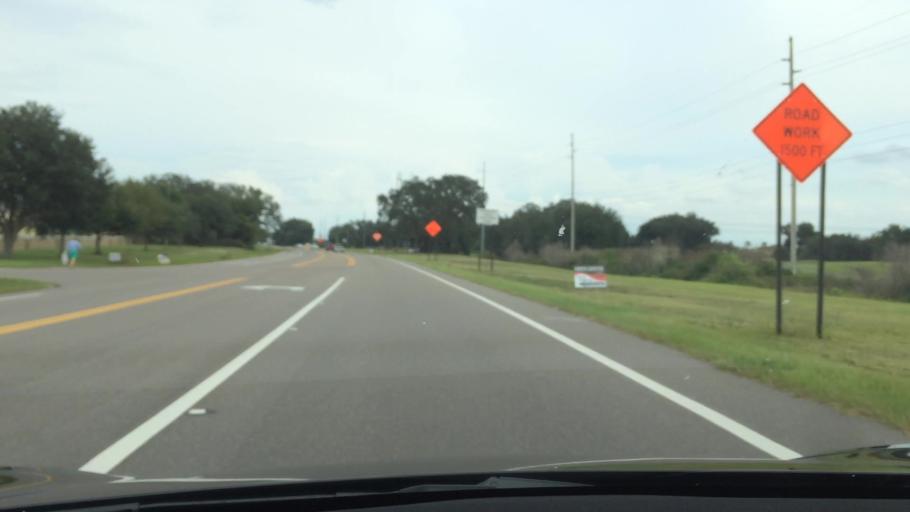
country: US
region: Florida
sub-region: Pasco County
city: Trinity
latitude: 28.1785
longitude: -82.6585
